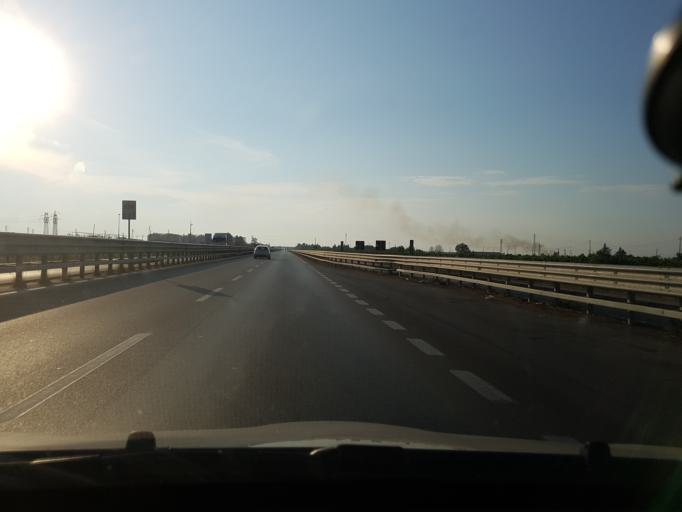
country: IT
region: Apulia
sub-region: Provincia di Foggia
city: Orta Nova
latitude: 41.3545
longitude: 15.7202
